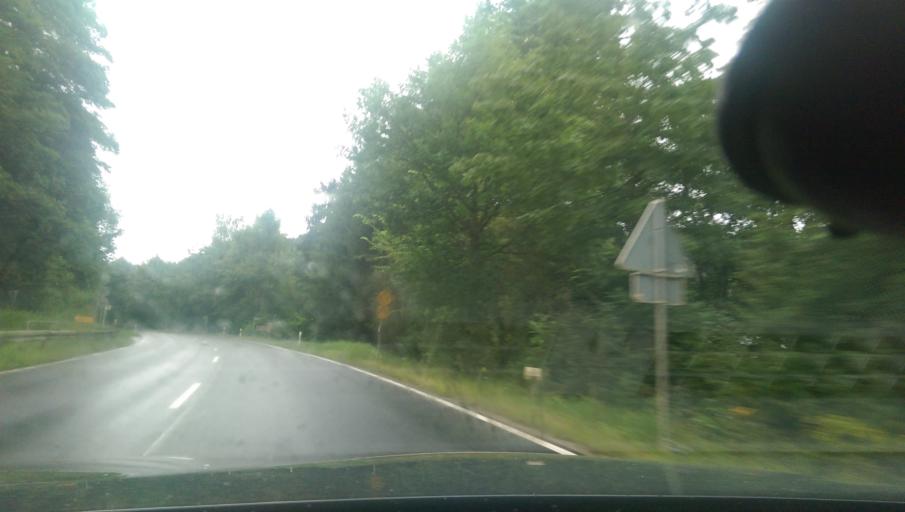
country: DE
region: Hesse
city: Witzenhausen
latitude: 51.3098
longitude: 9.8528
